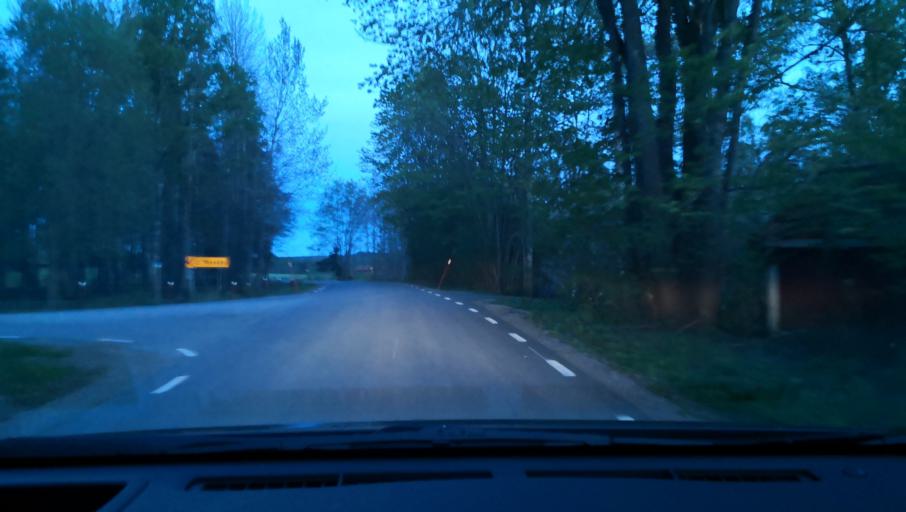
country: SE
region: OErebro
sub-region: Askersunds Kommun
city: Asbro
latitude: 59.0695
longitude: 14.9659
